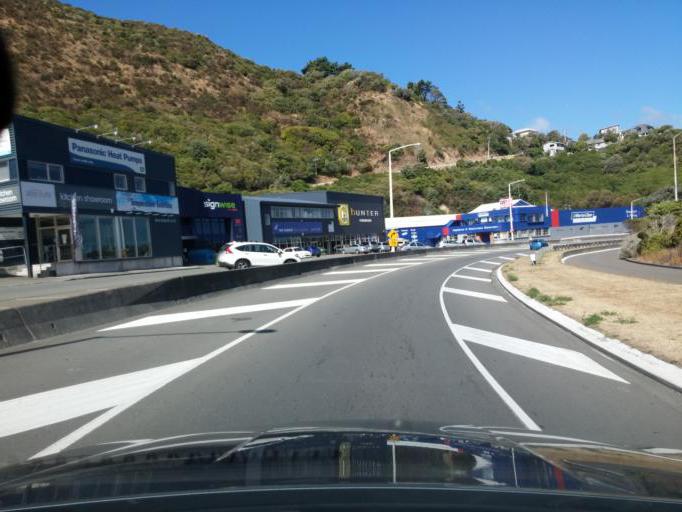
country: NZ
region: Wellington
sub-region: Wellington City
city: Wellington
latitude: -41.2426
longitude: 174.8132
